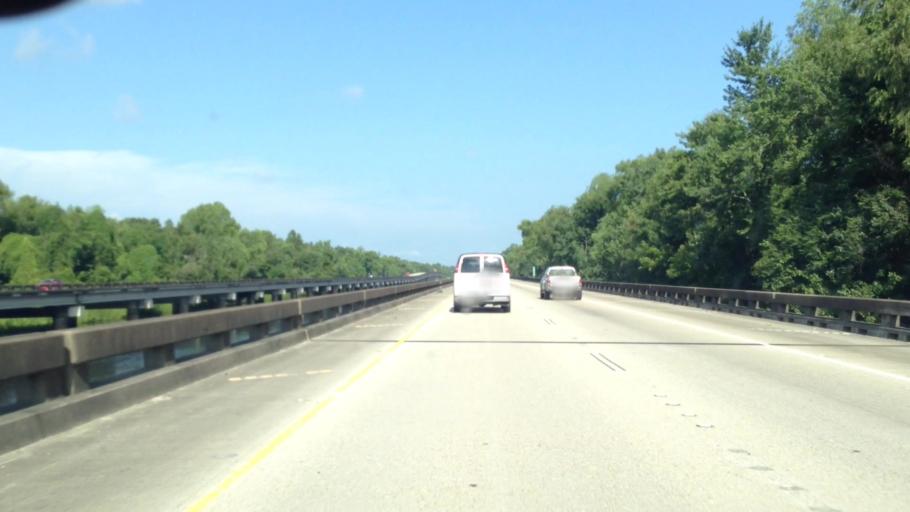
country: US
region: Louisiana
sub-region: Saint John the Baptist Parish
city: Montegut
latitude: 30.1106
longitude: -90.5366
